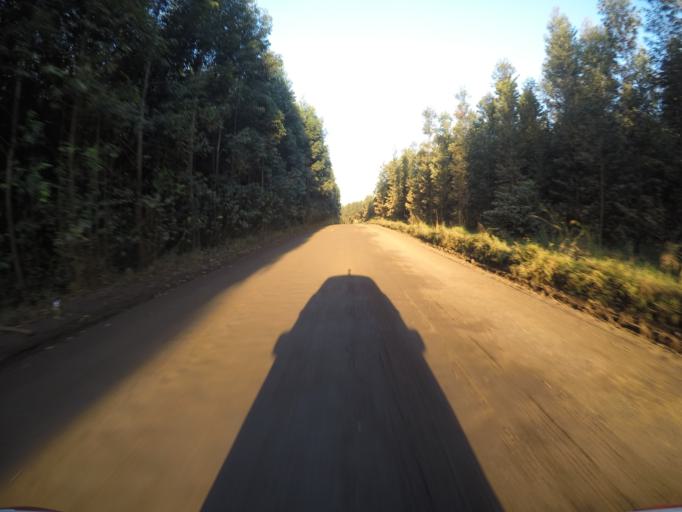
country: ZA
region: KwaZulu-Natal
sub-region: uThungulu District Municipality
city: KwaMbonambi
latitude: -28.6746
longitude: 32.1119
